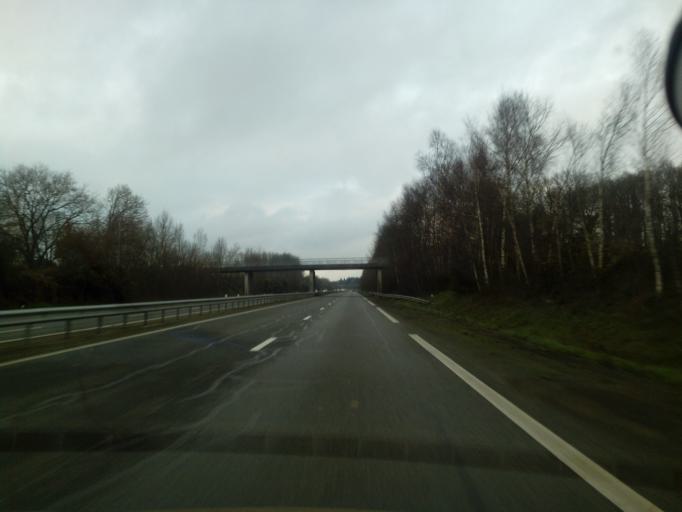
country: FR
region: Brittany
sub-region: Departement d'Ille-et-Vilaine
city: Saint-Meen-le-Grand
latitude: 48.1823
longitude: -2.2059
